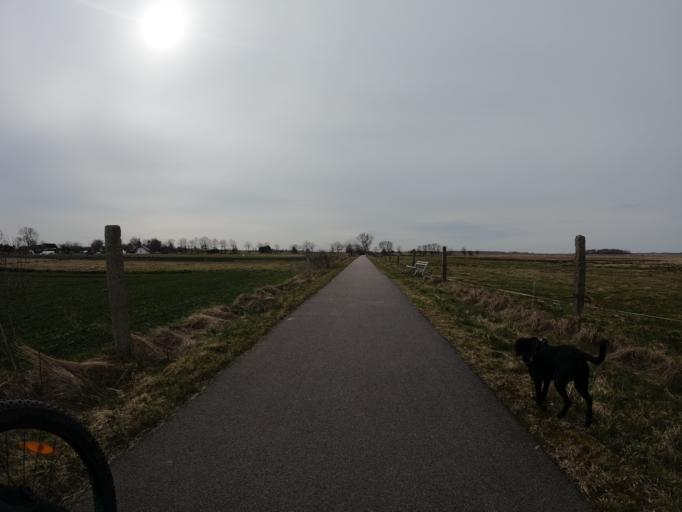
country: PL
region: West Pomeranian Voivodeship
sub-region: Powiat gryficki
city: Mrzezyno
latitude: 54.1259
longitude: 15.3146
